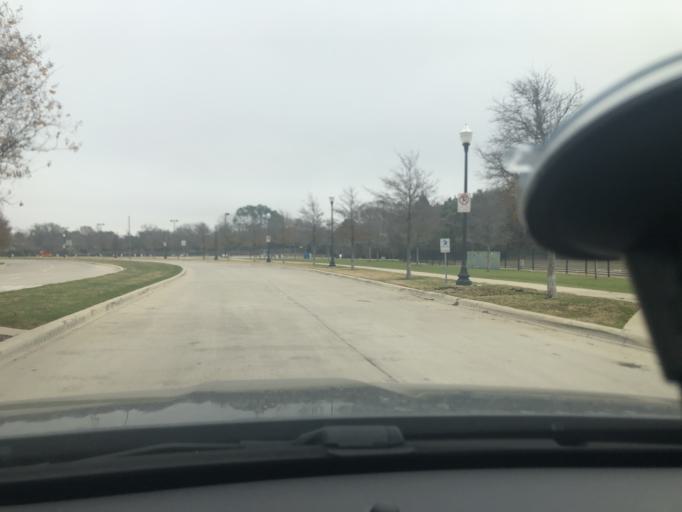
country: US
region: Texas
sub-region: Tarrant County
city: Westworth
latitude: 32.7360
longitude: -97.3697
